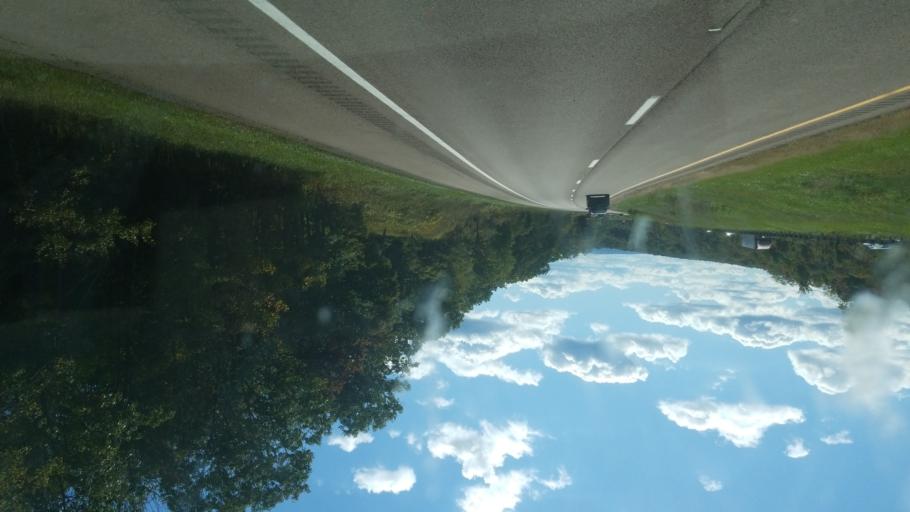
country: US
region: Maryland
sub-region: Garrett County
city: Oakland
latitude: 39.6941
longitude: -79.3415
